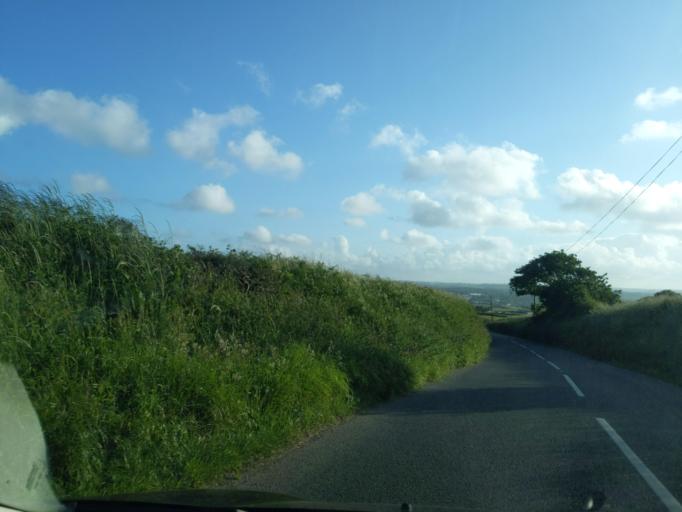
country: GB
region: England
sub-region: Devon
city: Great Torrington
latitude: 50.9654
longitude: -4.1176
